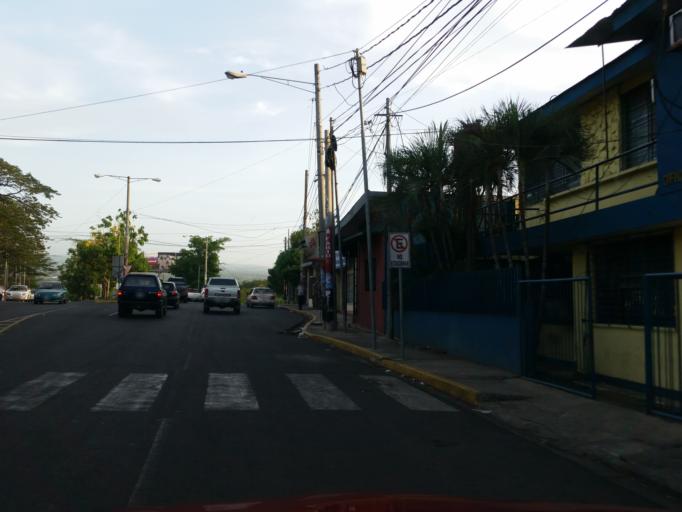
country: NI
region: Managua
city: Managua
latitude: 12.1398
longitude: -86.2755
